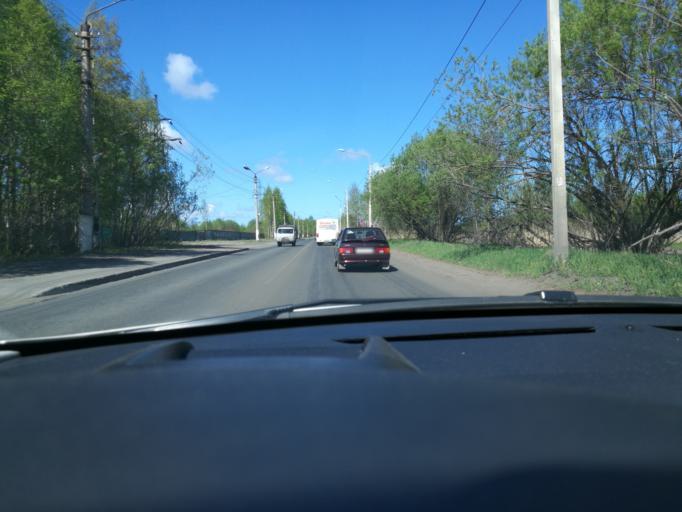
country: RU
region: Arkhangelskaya
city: Arkhangel'sk
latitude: 64.5970
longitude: 40.5640
